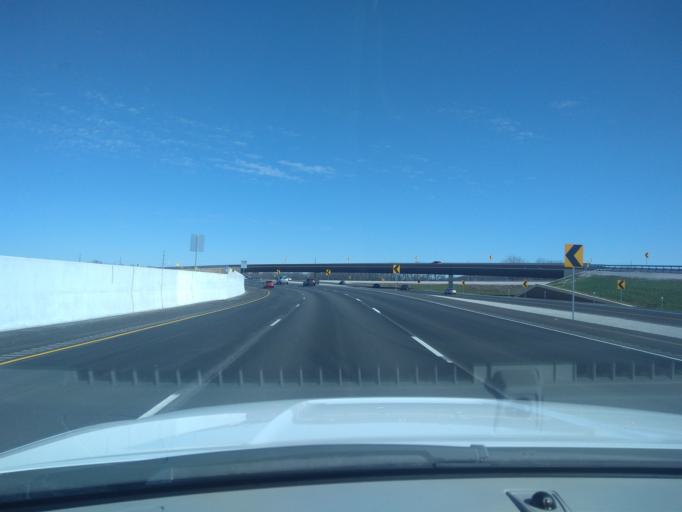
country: US
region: Arkansas
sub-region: Washington County
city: Johnson
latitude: 36.1072
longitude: -94.1738
